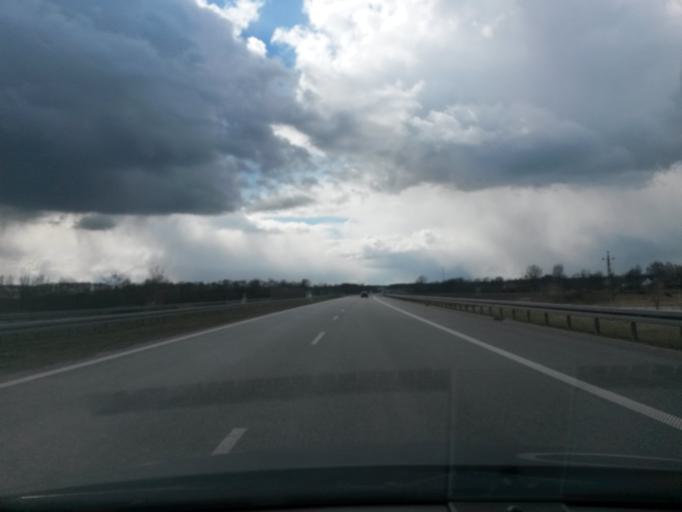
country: PL
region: Greater Poland Voivodeship
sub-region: Powiat koninski
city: Krzymow
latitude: 52.1433
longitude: 18.4046
